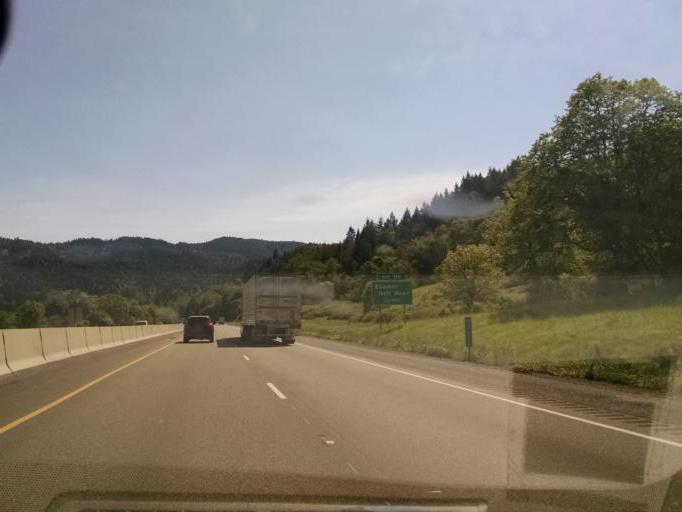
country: US
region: Oregon
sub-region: Douglas County
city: Myrtle Creek
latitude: 43.0468
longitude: -123.3320
